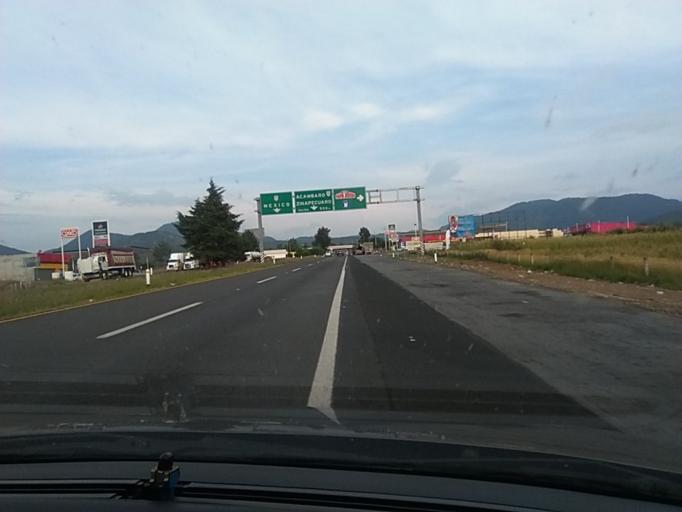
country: MX
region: Michoacan
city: Zinapecuaro
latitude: 19.9026
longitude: -100.7943
